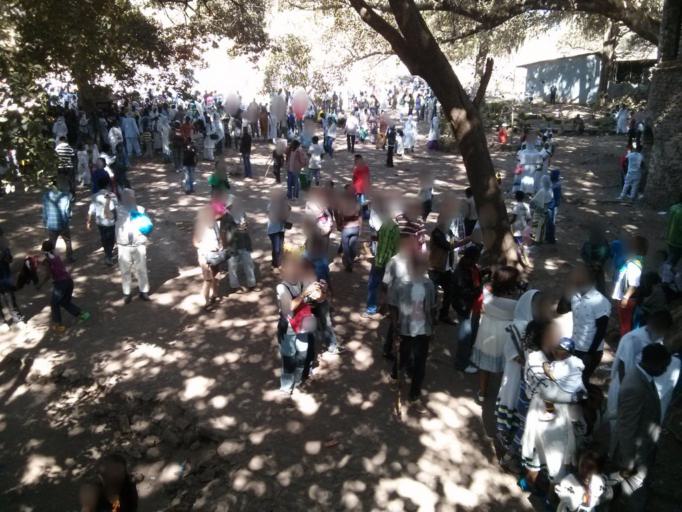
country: ET
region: Amhara
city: Gondar
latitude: 12.6175
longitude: 37.4576
